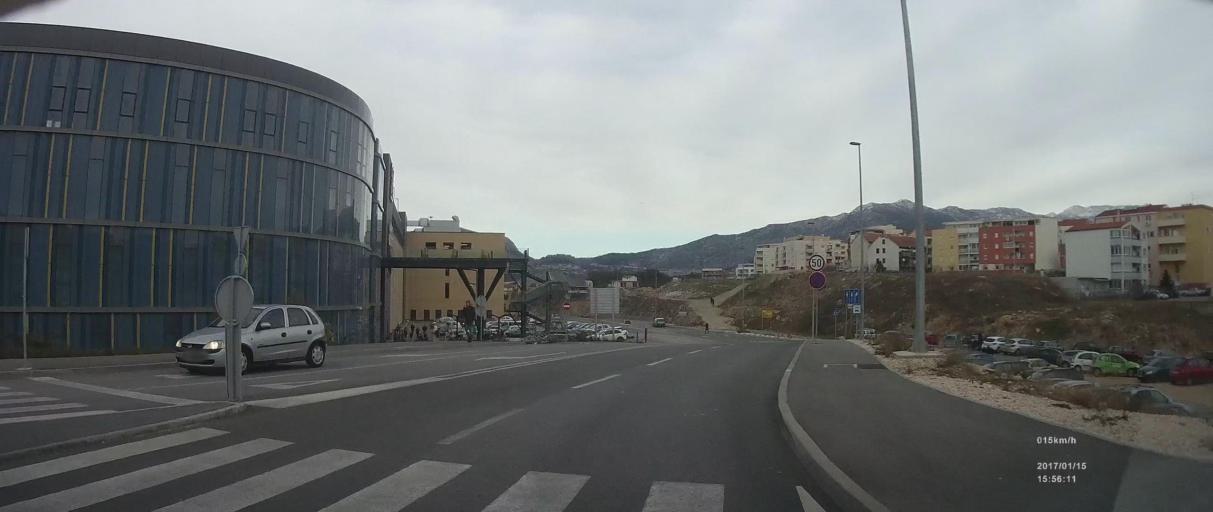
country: HR
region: Splitsko-Dalmatinska
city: Vranjic
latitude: 43.5178
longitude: 16.4842
